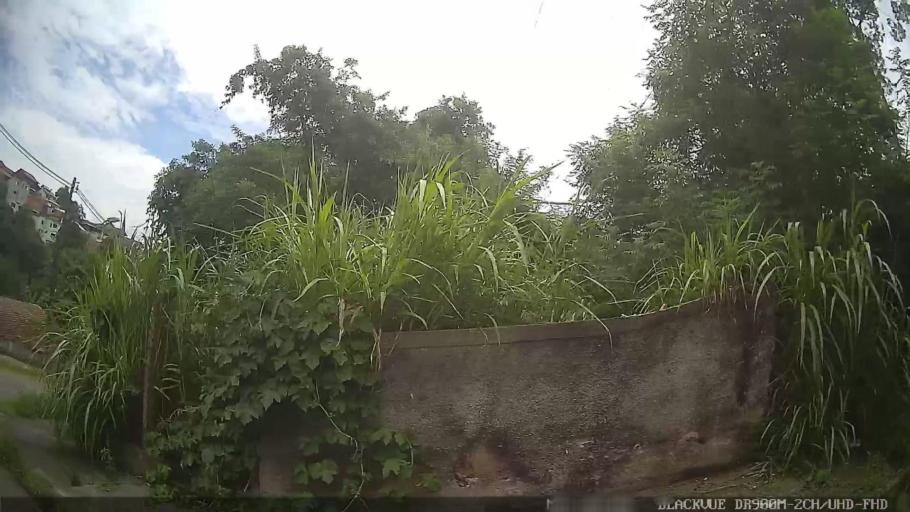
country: BR
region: Sao Paulo
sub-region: Ribeirao Pires
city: Ribeirao Pires
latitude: -23.7177
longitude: -46.4177
